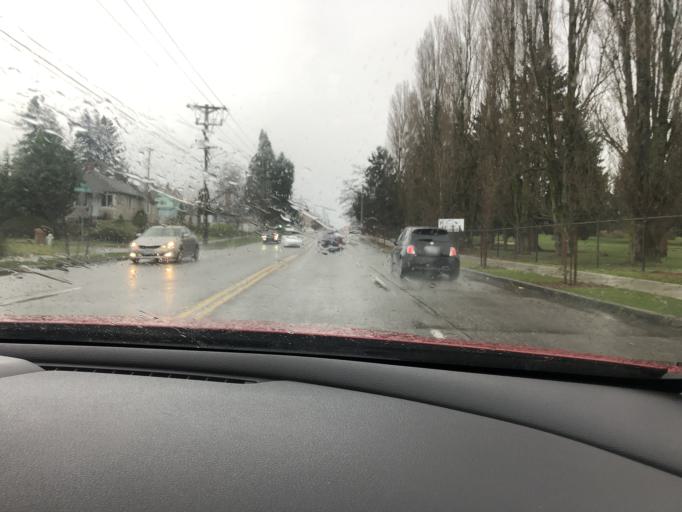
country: US
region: Washington
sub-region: Pierce County
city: Tacoma
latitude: 47.2427
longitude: -122.4723
